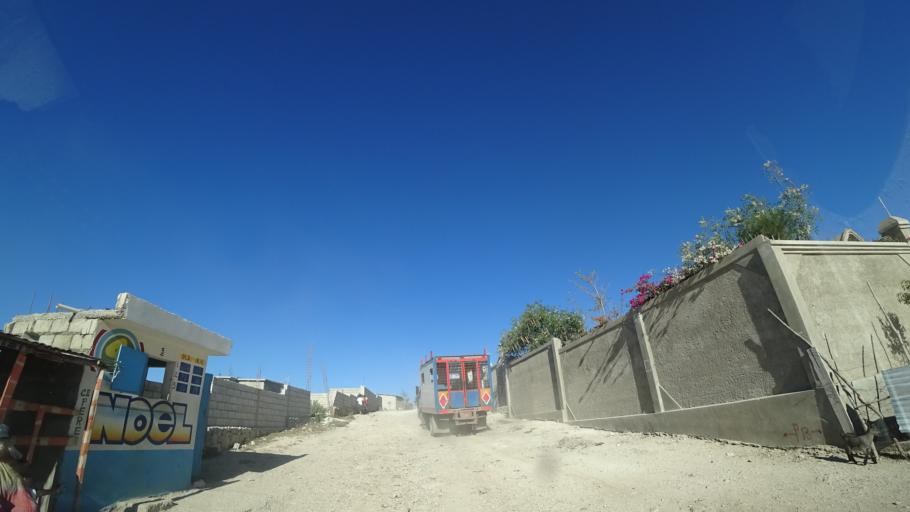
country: HT
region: Ouest
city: Cabaret
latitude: 18.6865
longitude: -72.3217
